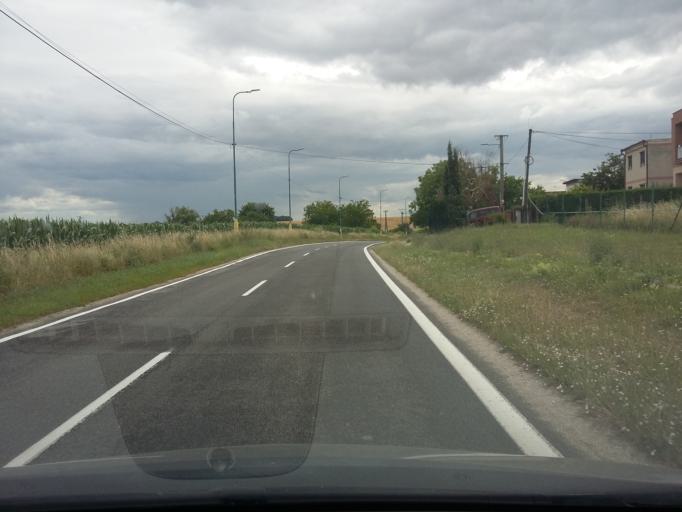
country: SK
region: Trnavsky
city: Vrbove
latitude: 48.6151
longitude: 17.7191
